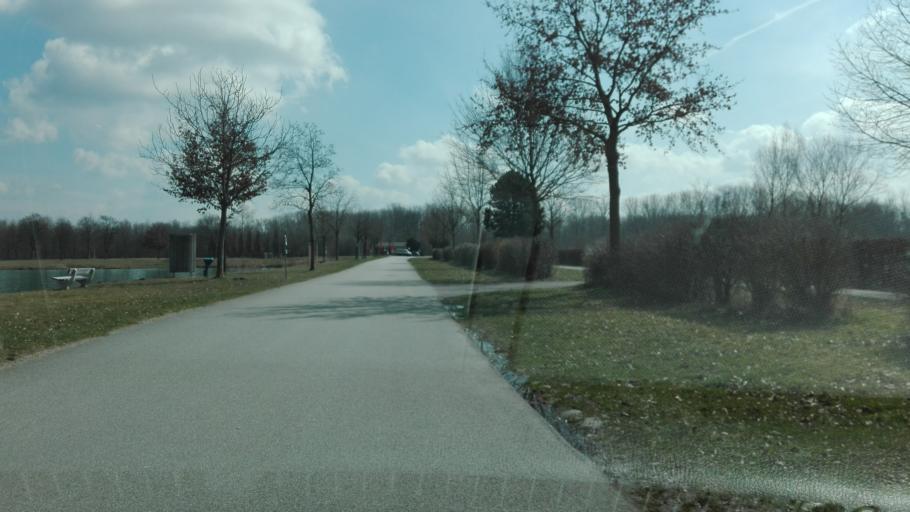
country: AT
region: Upper Austria
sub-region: Politischer Bezirk Urfahr-Umgebung
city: Feldkirchen an der Donau
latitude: 48.3255
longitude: 14.0719
